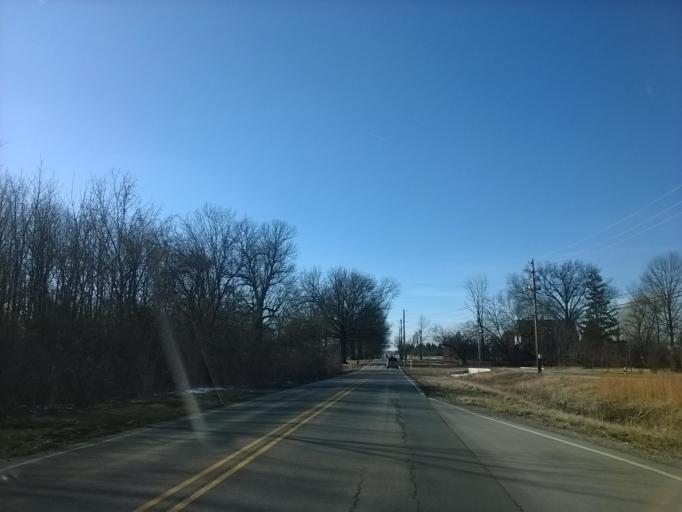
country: US
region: Indiana
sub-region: Boone County
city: Zionsville
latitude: 39.9409
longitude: -86.2257
